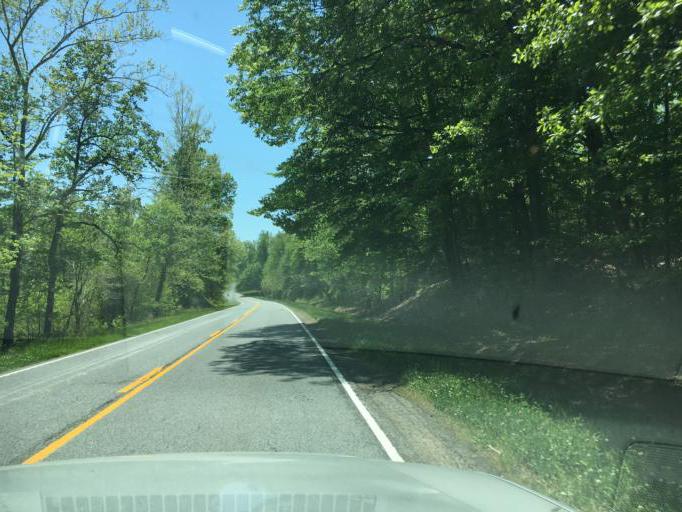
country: US
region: South Carolina
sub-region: Cherokee County
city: Blacksburg
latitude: 35.1348
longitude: -81.5822
